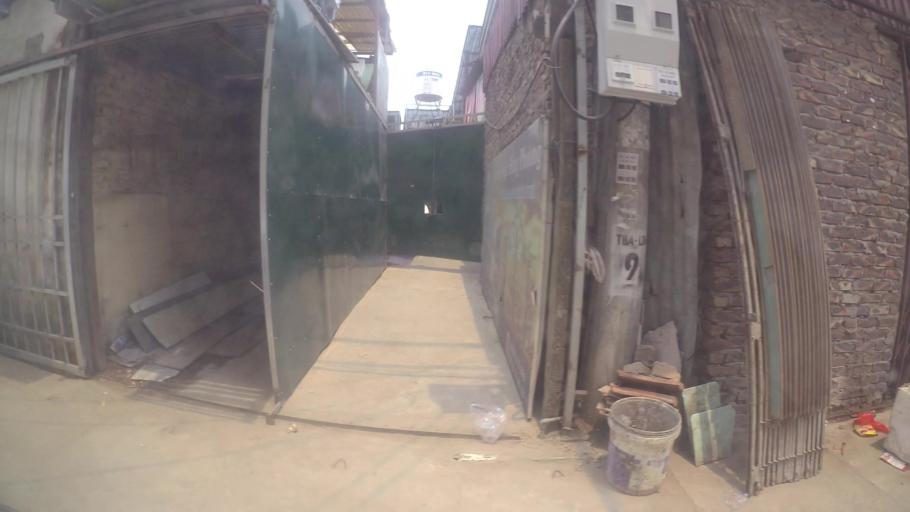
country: VN
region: Ha Noi
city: Ha Dong
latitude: 20.9919
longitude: 105.7410
